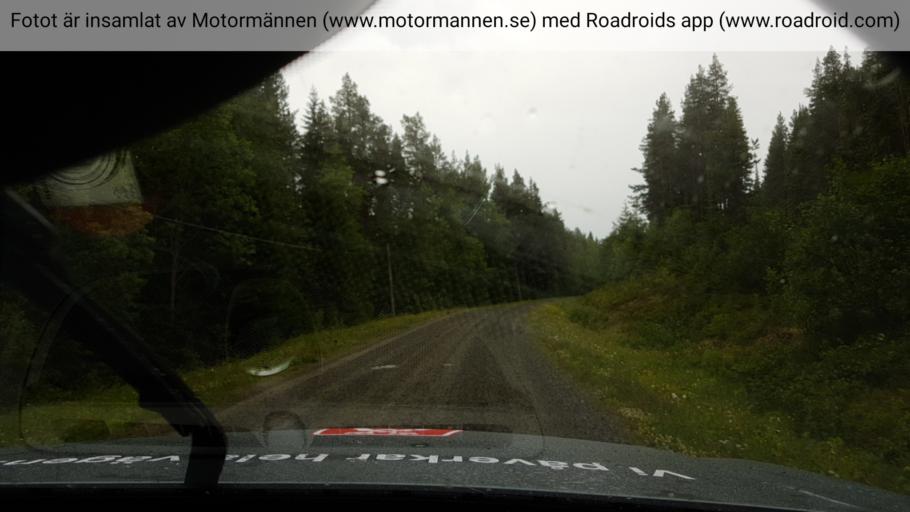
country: SE
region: Jaemtland
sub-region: Bergs Kommun
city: Hoverberg
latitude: 62.5278
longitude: 14.7117
